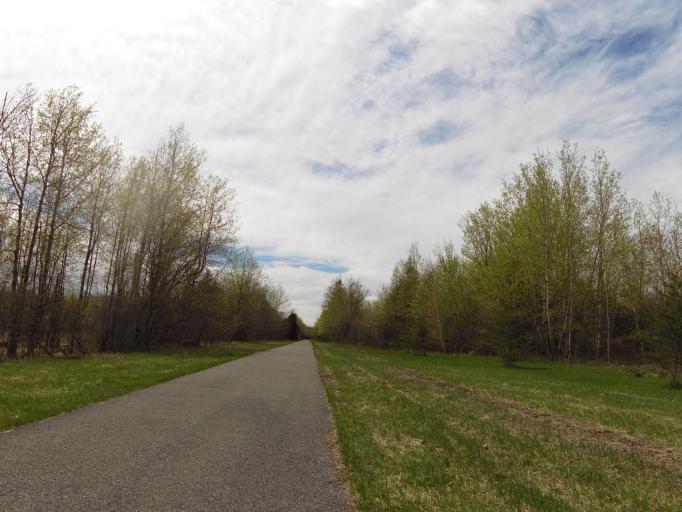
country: CA
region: Ontario
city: Hawkesbury
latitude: 45.5345
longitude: -74.6464
